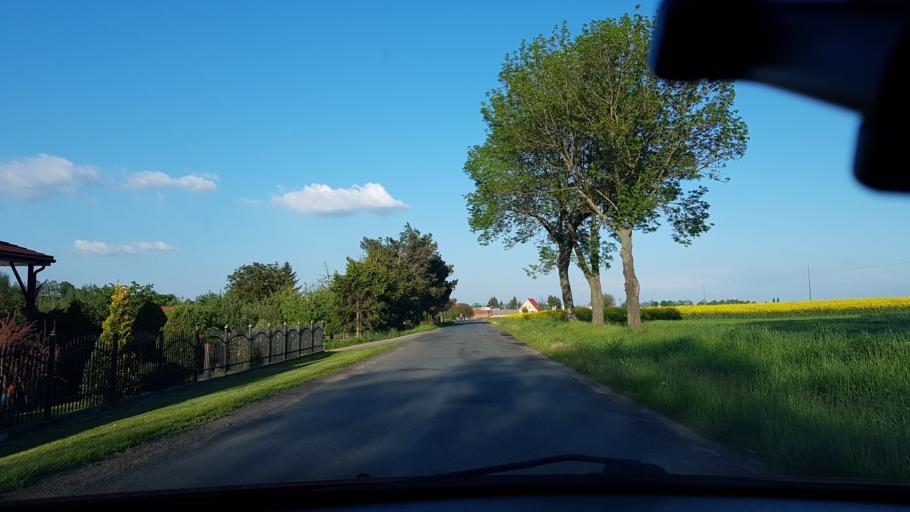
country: PL
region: Lower Silesian Voivodeship
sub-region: Powiat zabkowicki
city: Budzow
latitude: 50.6073
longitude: 16.7184
